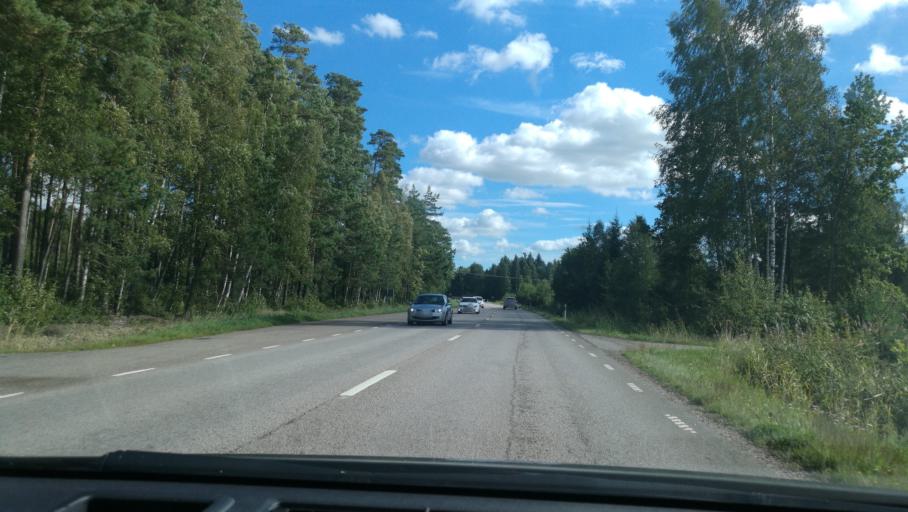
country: SE
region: Vaestra Goetaland
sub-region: Lidkopings Kommun
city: Vinninga
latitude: 58.4912
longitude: 13.2754
